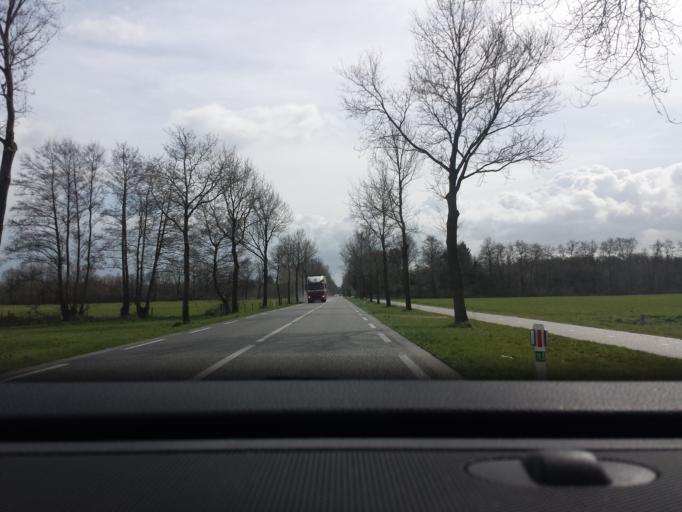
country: NL
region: Gelderland
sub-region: Oude IJsselstreek
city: Varsseveld
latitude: 51.9642
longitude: 6.4502
